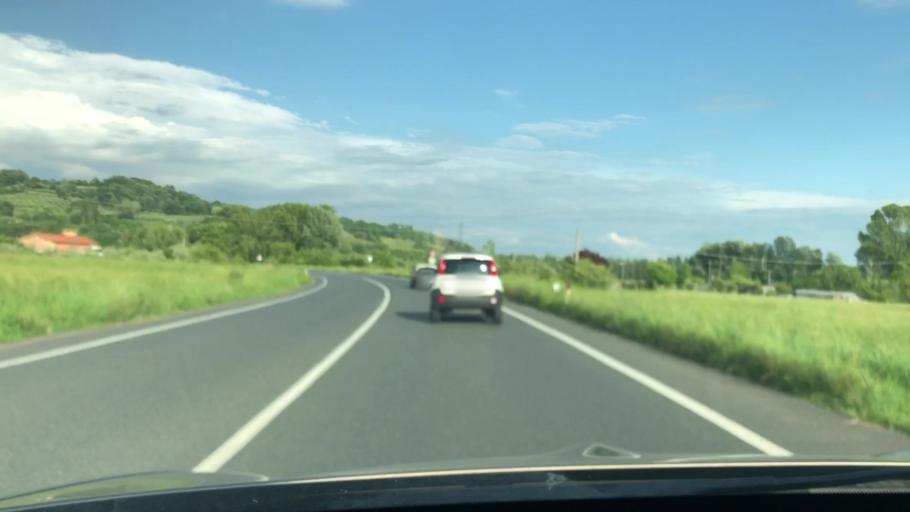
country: IT
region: Tuscany
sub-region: Province of Pisa
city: Treggiaia
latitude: 43.6187
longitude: 10.6695
